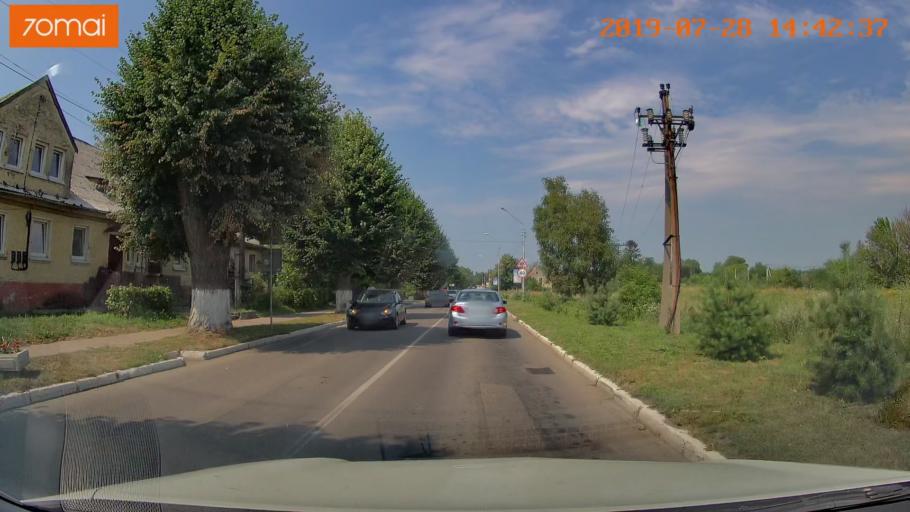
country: RU
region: Kaliningrad
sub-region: Gorod Kaliningrad
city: Yantarnyy
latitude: 54.8610
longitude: 19.9414
